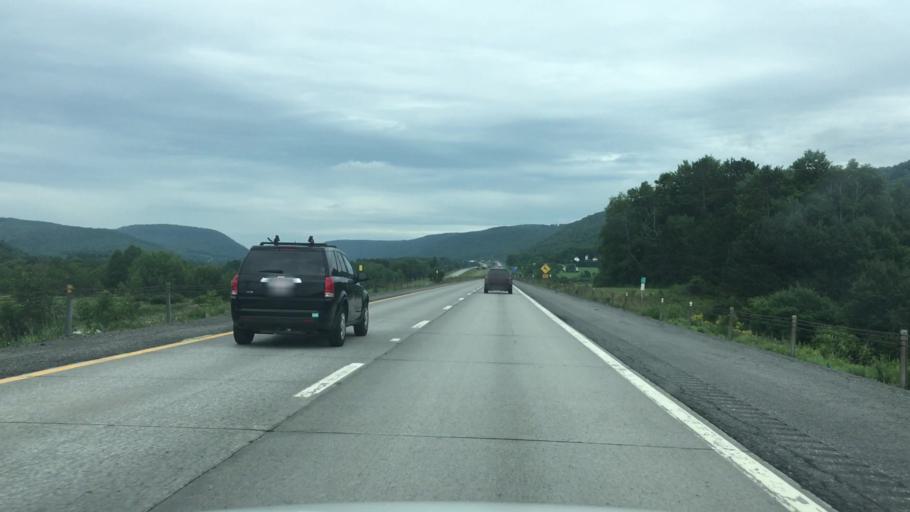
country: US
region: New York
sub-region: Otsego County
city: Worcester
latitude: 42.5331
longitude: -74.8608
